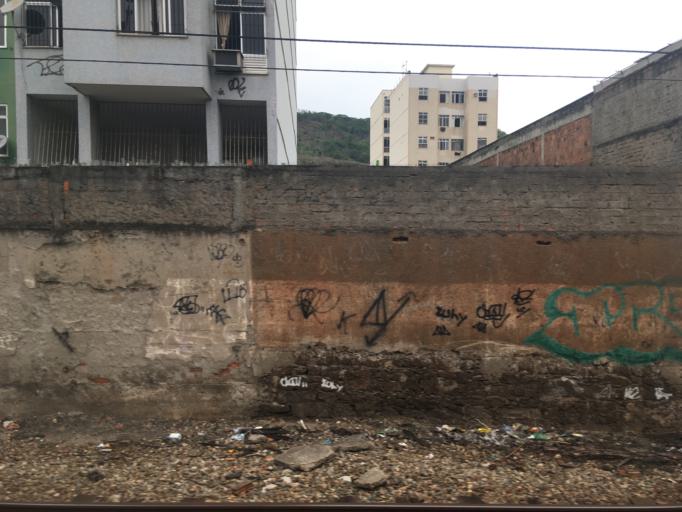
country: BR
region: Rio de Janeiro
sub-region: Rio De Janeiro
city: Rio de Janeiro
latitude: -22.9011
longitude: -43.2524
